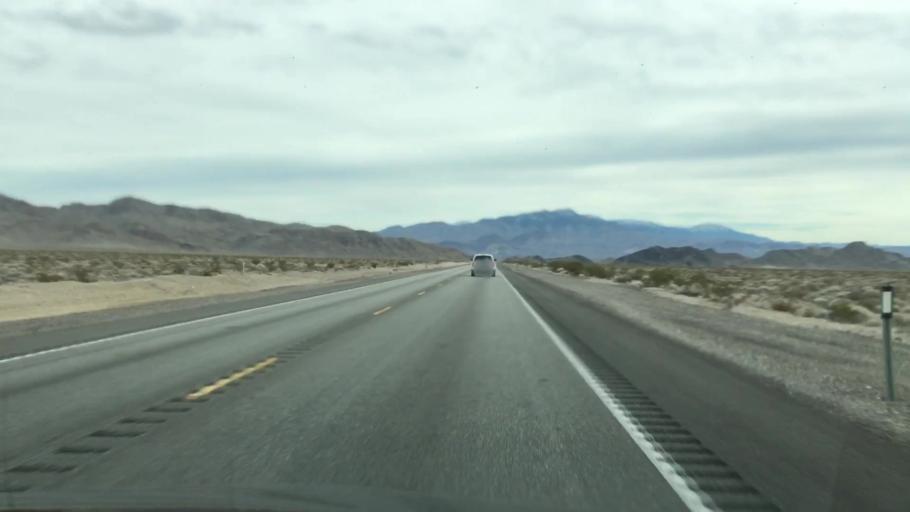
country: US
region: Nevada
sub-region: Nye County
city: Pahrump
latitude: 36.6009
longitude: -116.2485
